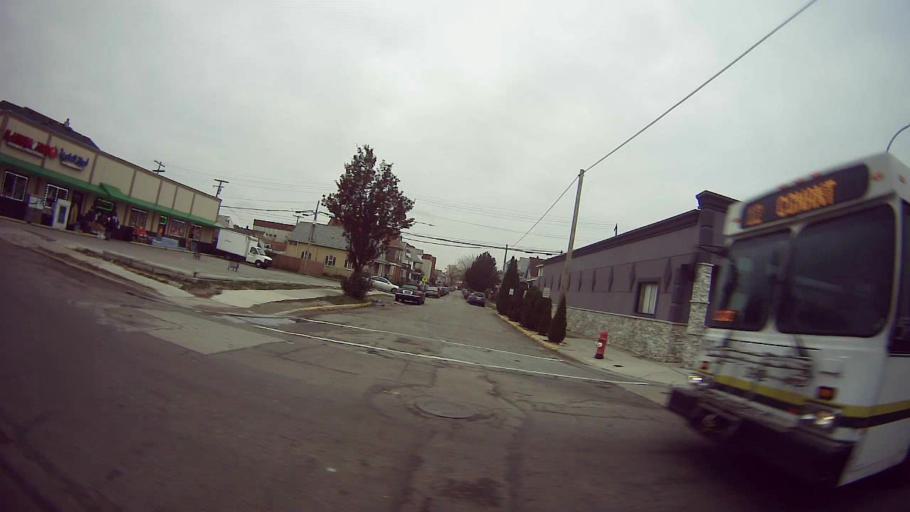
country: US
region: Michigan
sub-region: Wayne County
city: Hamtramck
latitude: 42.3991
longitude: -83.0504
